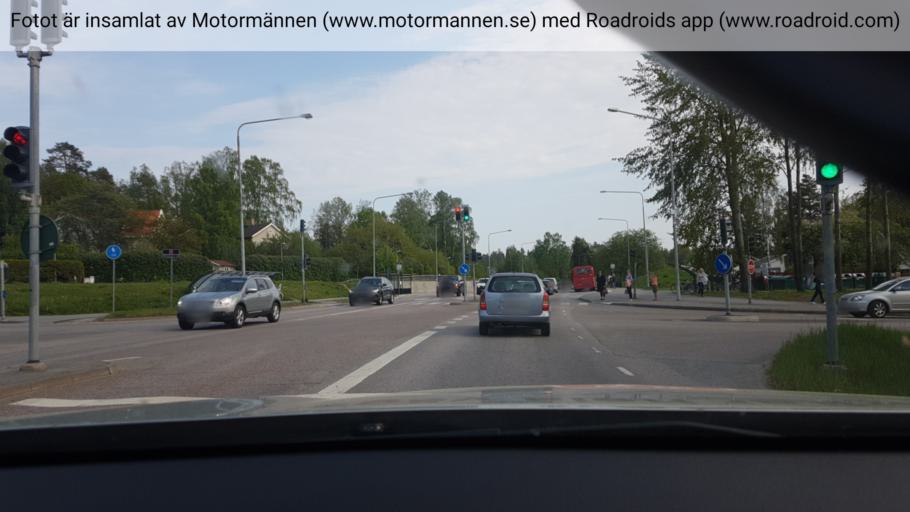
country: SE
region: Stockholm
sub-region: Tyreso Kommun
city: Bollmora
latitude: 59.2145
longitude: 18.2078
